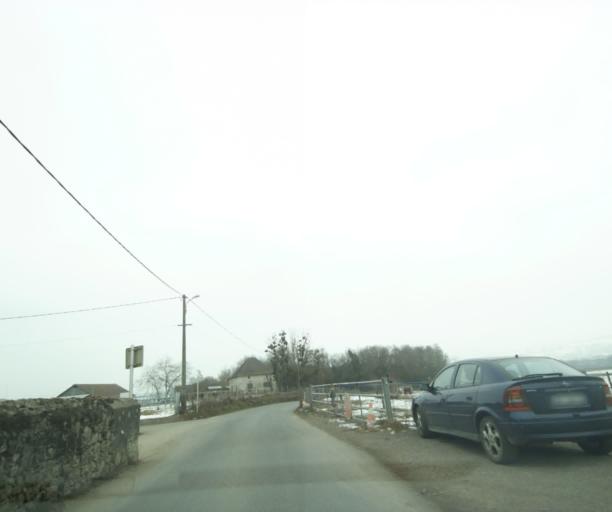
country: FR
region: Rhone-Alpes
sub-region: Departement de la Haute-Savoie
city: Reignier-Esery
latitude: 46.1276
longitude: 6.2840
